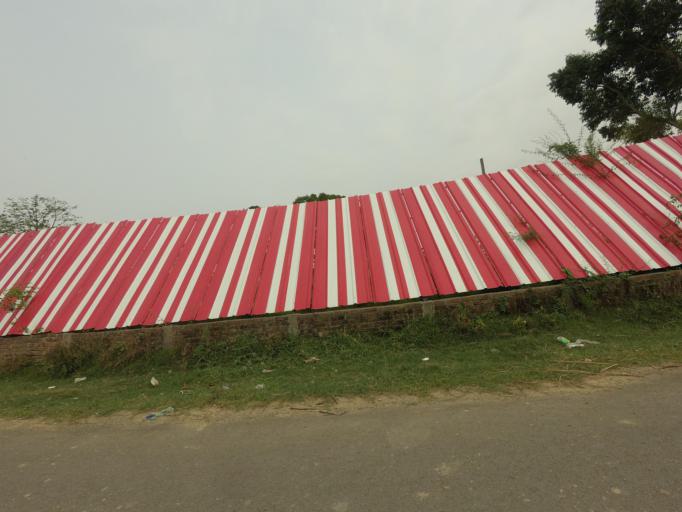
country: NP
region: Western Region
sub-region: Lumbini Zone
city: Bhairahawa
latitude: 27.4855
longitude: 83.4271
